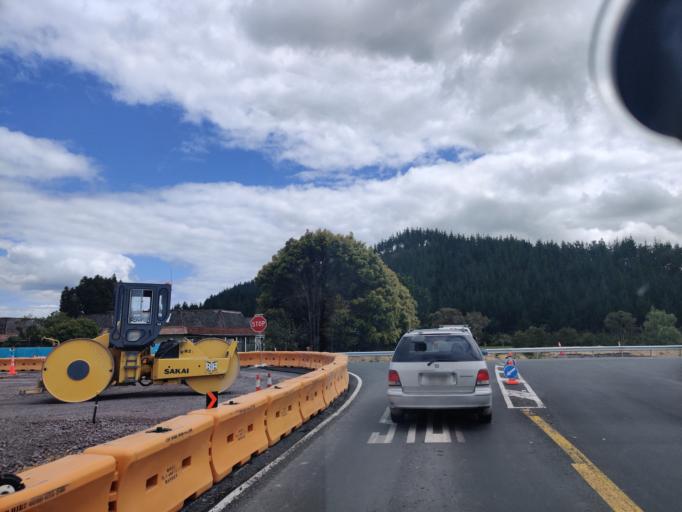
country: NZ
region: Northland
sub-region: Far North District
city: Kerikeri
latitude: -35.3031
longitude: 173.9622
